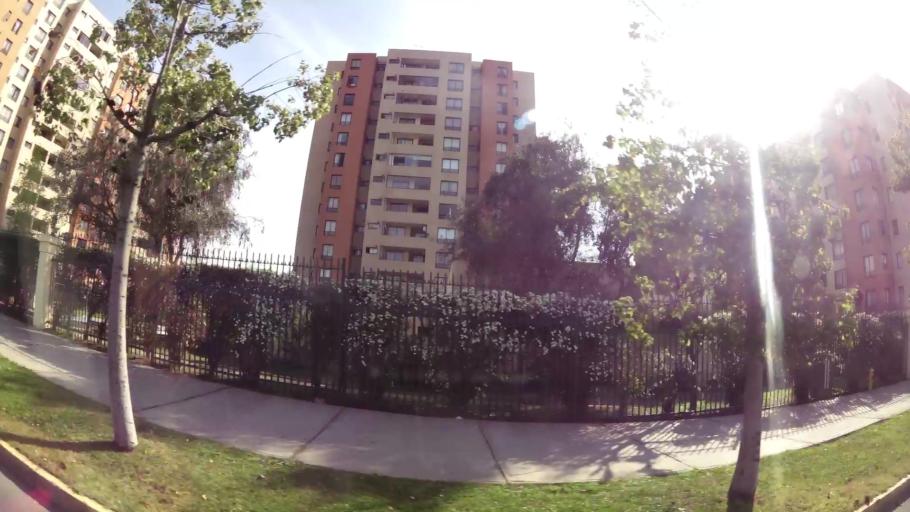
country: CL
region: Santiago Metropolitan
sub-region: Provincia de Santiago
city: Villa Presidente Frei, Nunoa, Santiago, Chile
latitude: -33.5275
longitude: -70.5885
